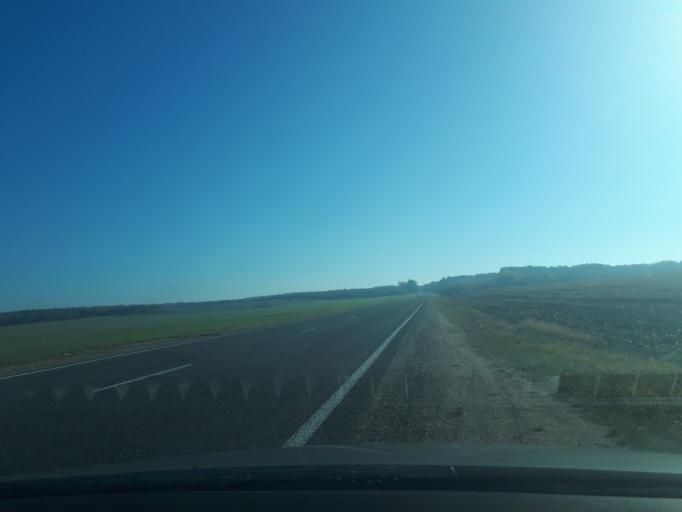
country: BY
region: Grodnenskaya
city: Zel'va
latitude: 53.1438
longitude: 24.8787
